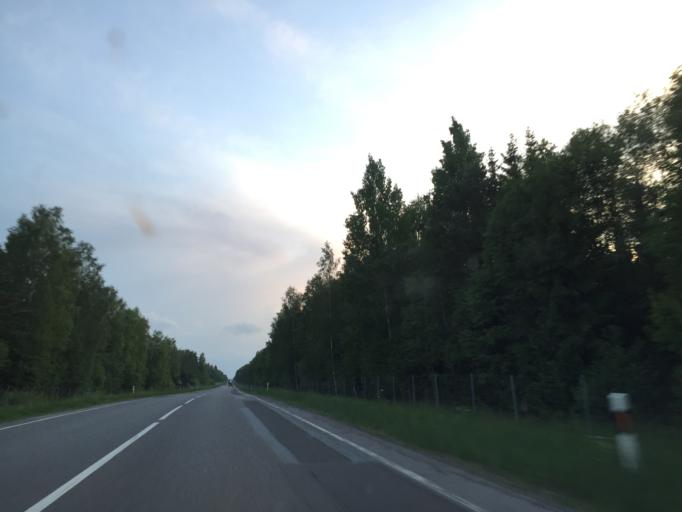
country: LT
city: Venta
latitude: 56.0003
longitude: 22.6342
